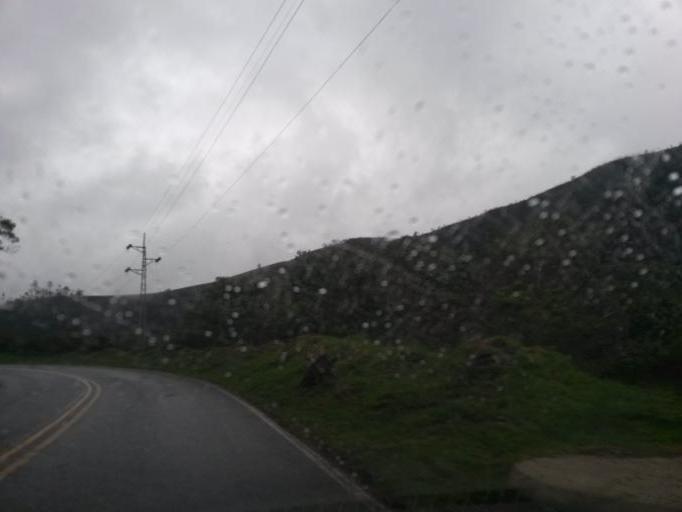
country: CO
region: Cauca
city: Popayan
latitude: 2.4044
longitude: -76.5018
